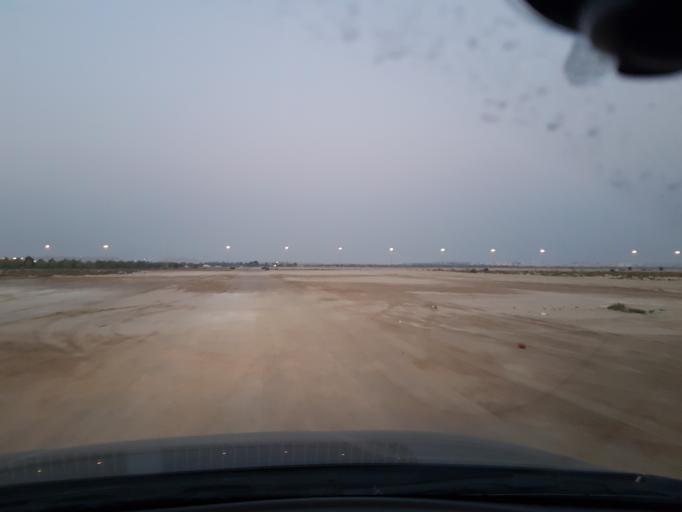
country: BH
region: Central Governorate
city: Dar Kulayb
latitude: 26.0100
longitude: 50.4796
